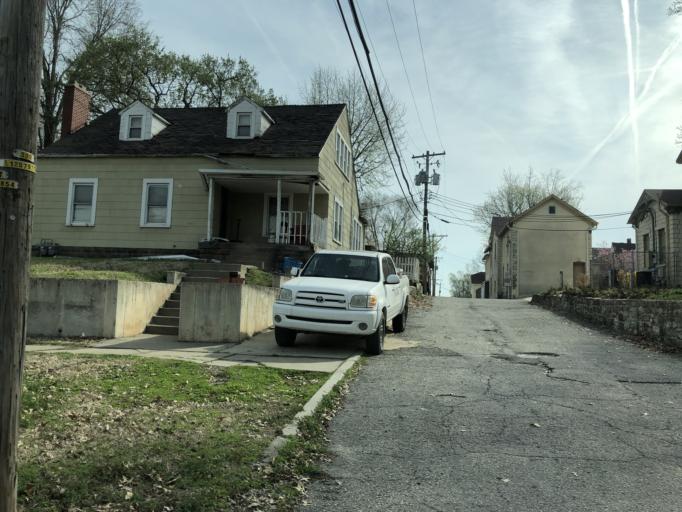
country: US
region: Kansas
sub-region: Leavenworth County
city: Leavenworth
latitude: 39.3119
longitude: -94.9172
